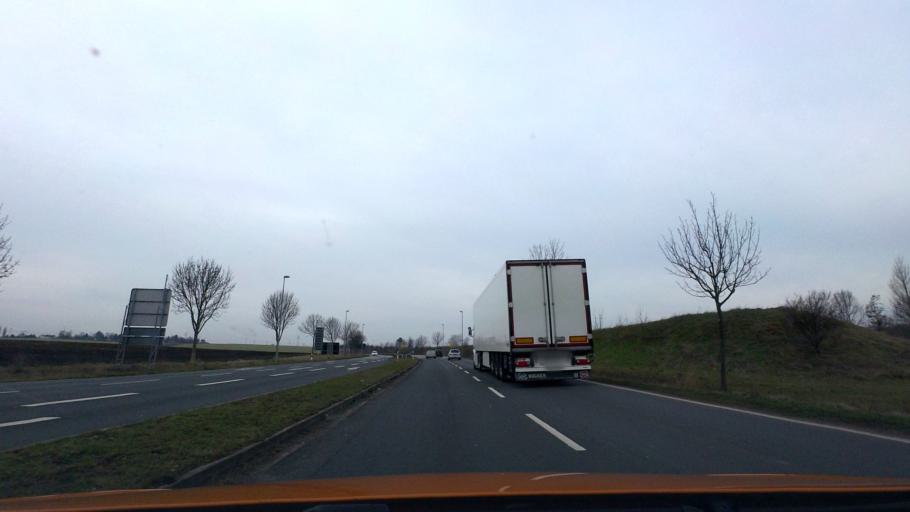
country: DE
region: Saxony-Anhalt
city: Diesdorf
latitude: 52.1417
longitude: 11.5722
